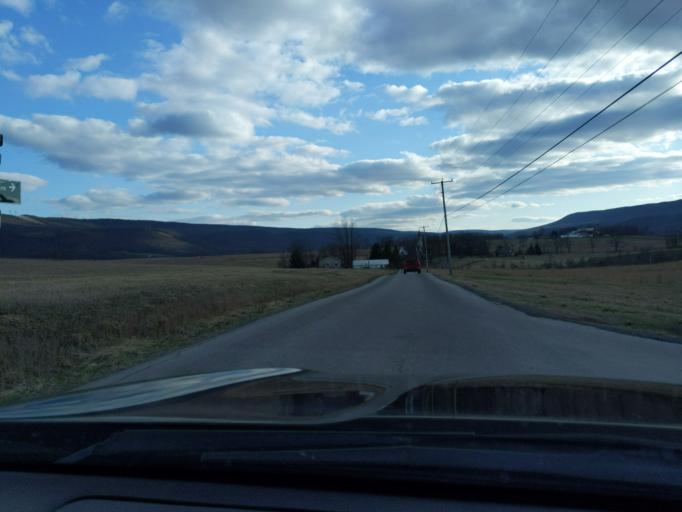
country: US
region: Pennsylvania
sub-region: Blair County
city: Tipton
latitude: 40.5983
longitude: -78.2482
